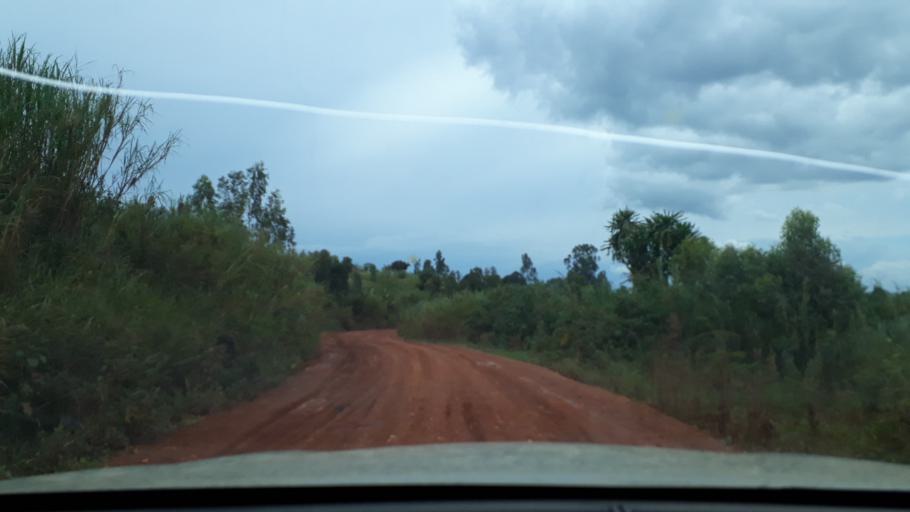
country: CD
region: Eastern Province
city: Bunia
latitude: 1.7541
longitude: 30.3736
